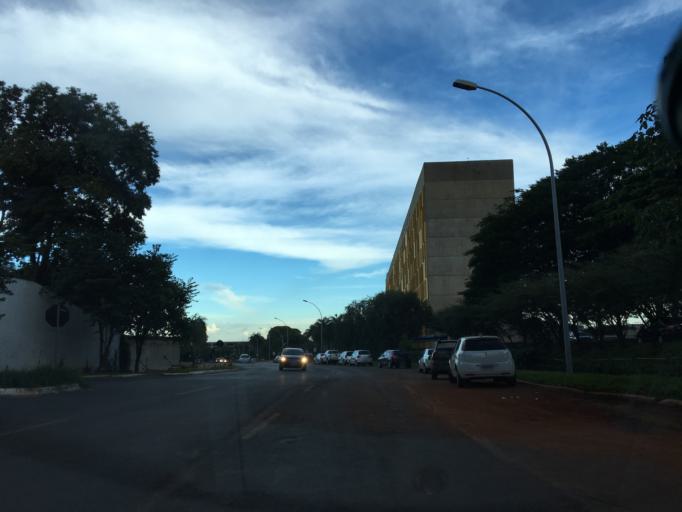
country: BR
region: Federal District
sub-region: Brasilia
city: Brasilia
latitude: -15.8018
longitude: -47.8674
